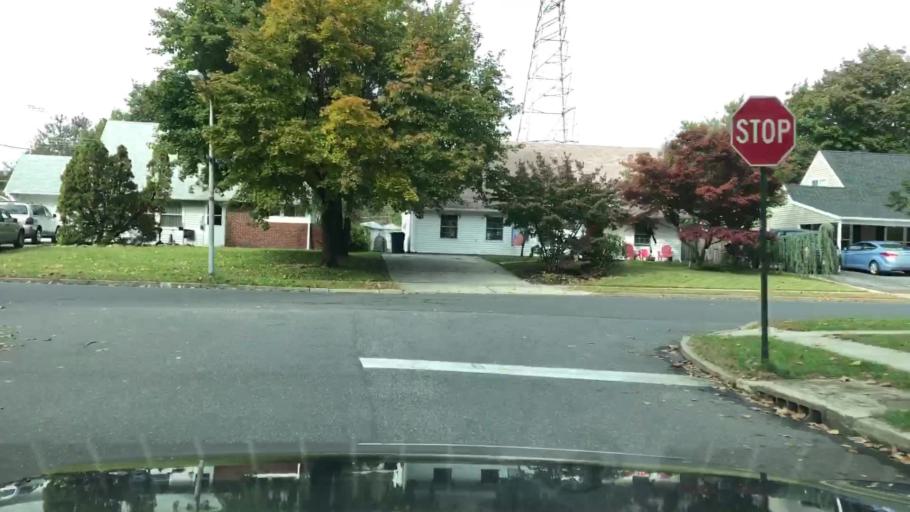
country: US
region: Pennsylvania
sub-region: Bucks County
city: Tullytown
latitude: 40.1427
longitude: -74.8249
